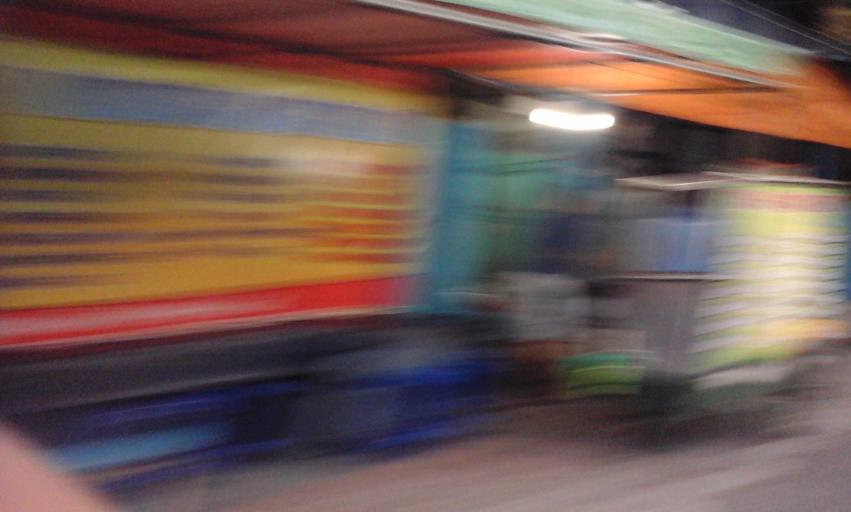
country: ID
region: East Java
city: Kepatihan
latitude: -8.1687
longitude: 113.7050
